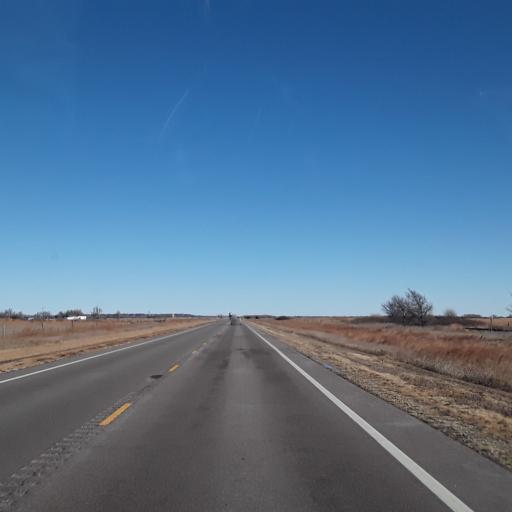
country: US
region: Kansas
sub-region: Pawnee County
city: Larned
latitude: 38.1363
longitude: -99.1557
